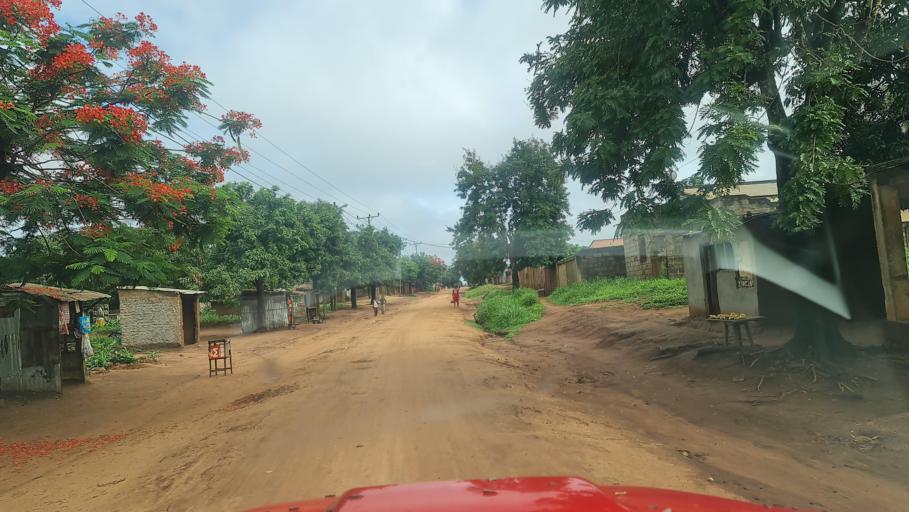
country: MW
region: Southern Region
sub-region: Nsanje District
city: Nsanje
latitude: -17.3244
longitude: 35.5916
